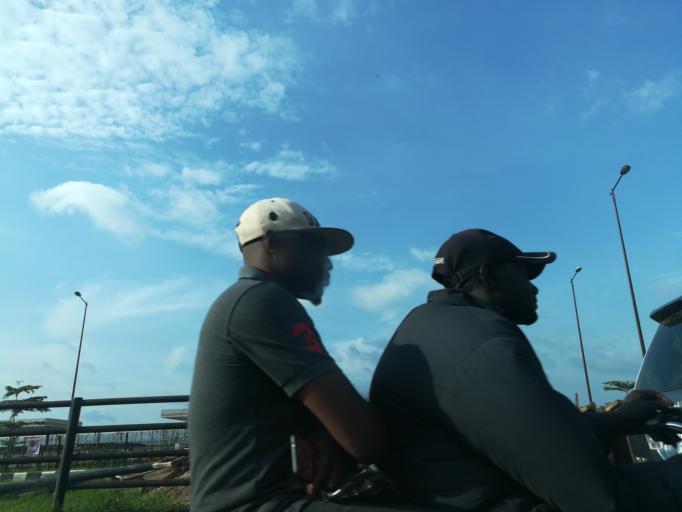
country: NG
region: Lagos
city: Ebute Ikorodu
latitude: 6.6093
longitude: 3.4323
